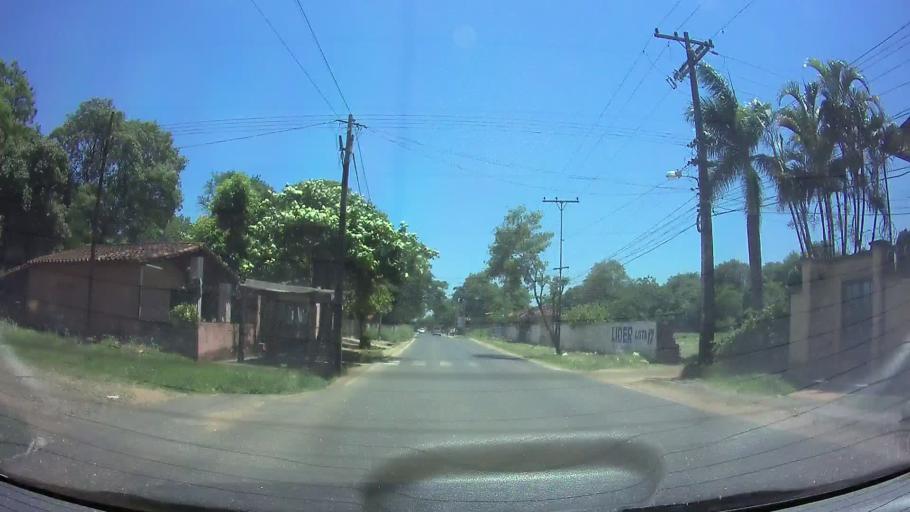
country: PY
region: Central
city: Fernando de la Mora
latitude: -25.2794
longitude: -57.5189
